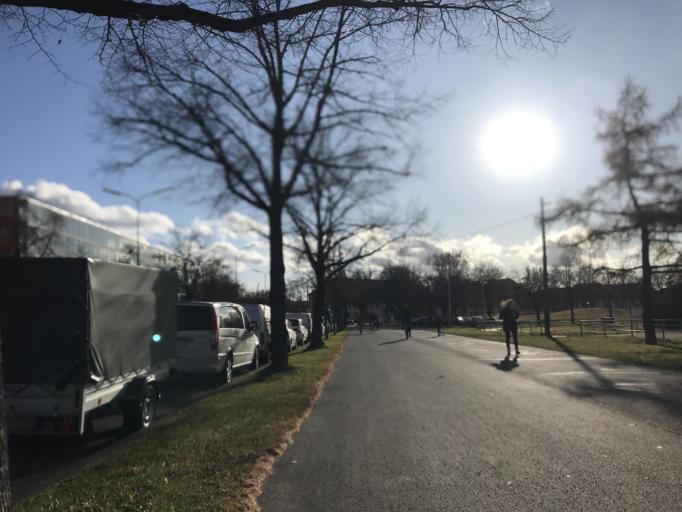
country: DE
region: Bavaria
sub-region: Upper Bavaria
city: Munich
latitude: 48.1632
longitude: 11.5528
